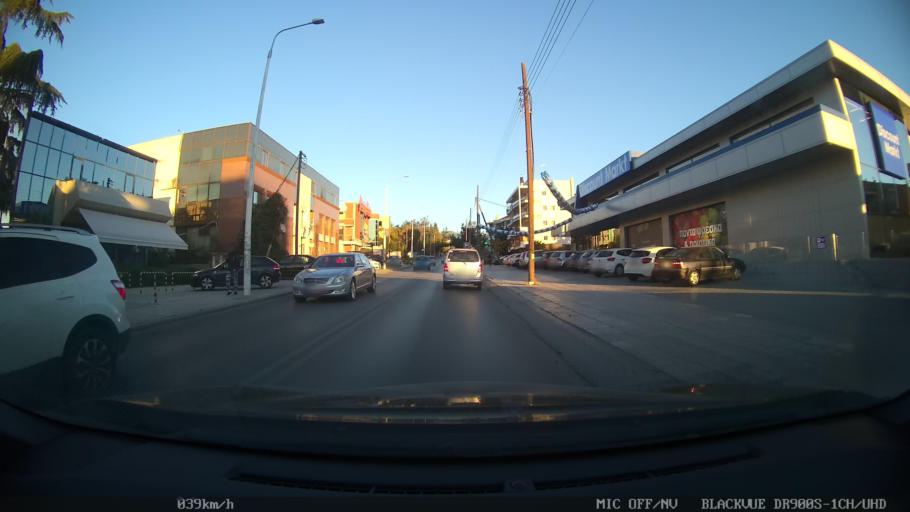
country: GR
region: Central Macedonia
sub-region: Nomos Thessalonikis
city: Pylaia
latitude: 40.6026
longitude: 22.9766
